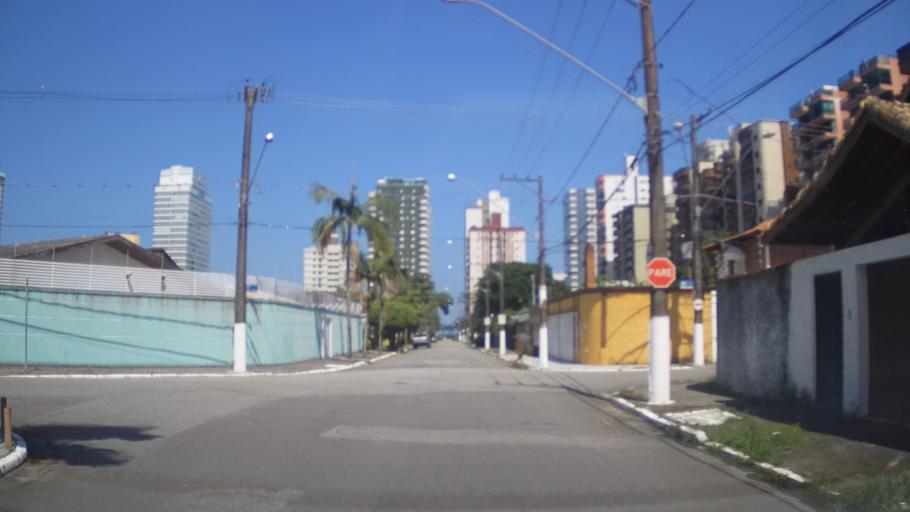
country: BR
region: Sao Paulo
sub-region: Praia Grande
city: Praia Grande
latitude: -24.0112
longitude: -46.4046
